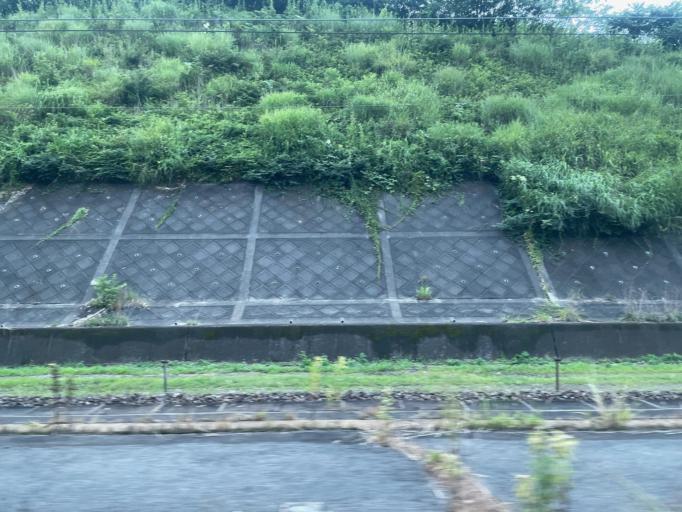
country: JP
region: Tochigi
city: Kuroiso
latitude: 37.0556
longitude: 140.1555
